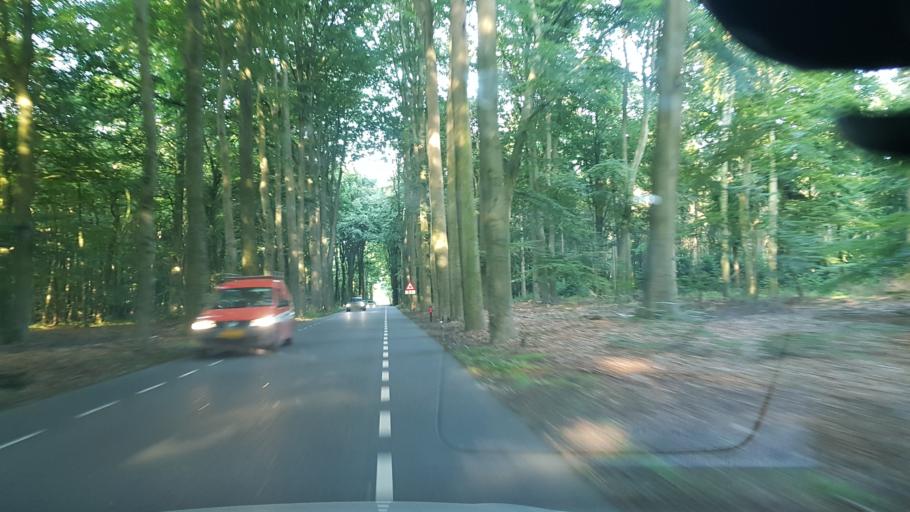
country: NL
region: Gelderland
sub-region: Gemeente Groesbeek
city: Groesbeek
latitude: 51.7746
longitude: 5.9220
